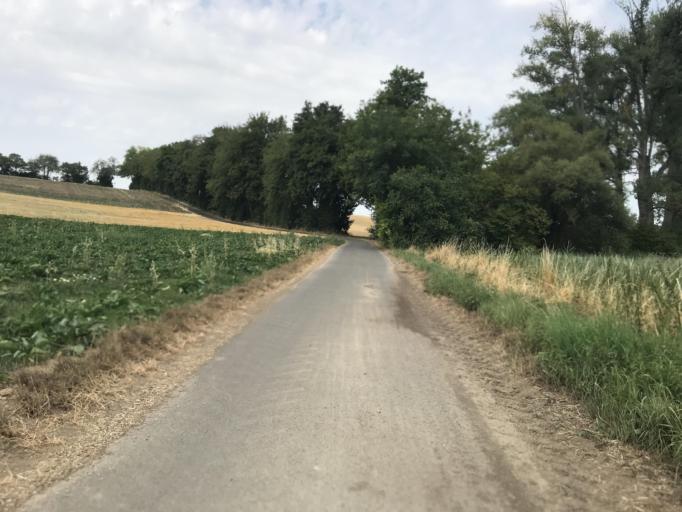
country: DE
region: Rheinland-Pfalz
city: Sorgenloch
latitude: 49.8632
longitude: 8.2060
